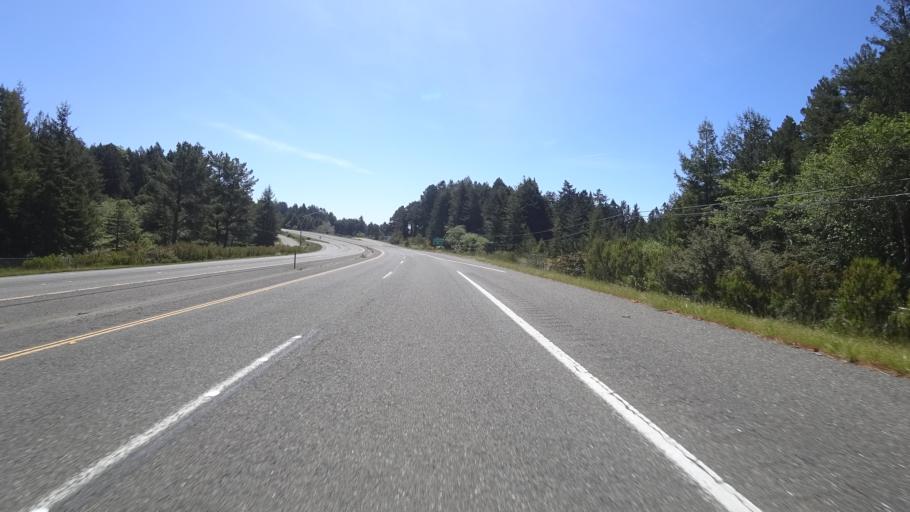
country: US
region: California
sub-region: Humboldt County
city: Westhaven-Moonstone
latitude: 41.0656
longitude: -124.1420
